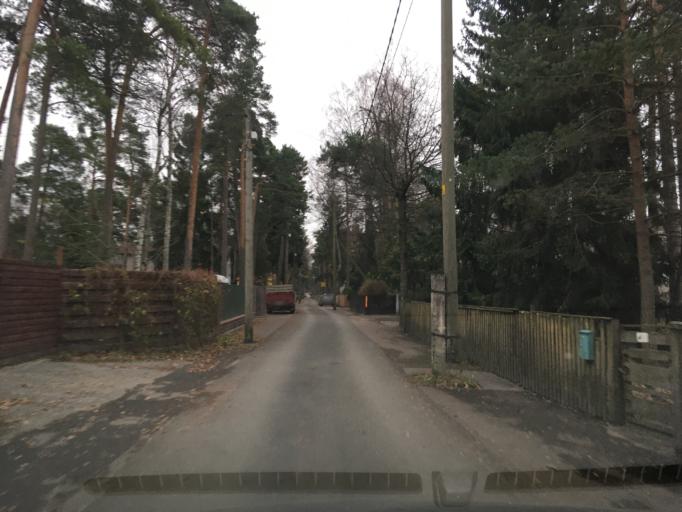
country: EE
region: Harju
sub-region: Saue vald
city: Laagri
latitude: 59.3845
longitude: 24.6801
